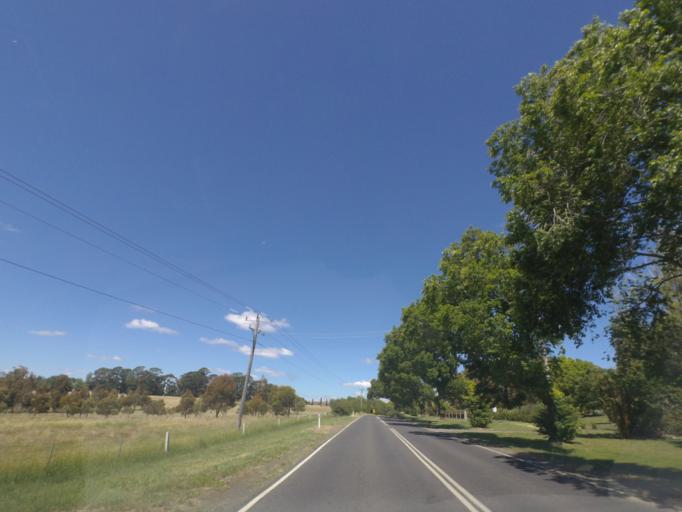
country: AU
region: Victoria
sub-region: Mount Alexander
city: Castlemaine
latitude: -37.2405
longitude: 144.4332
